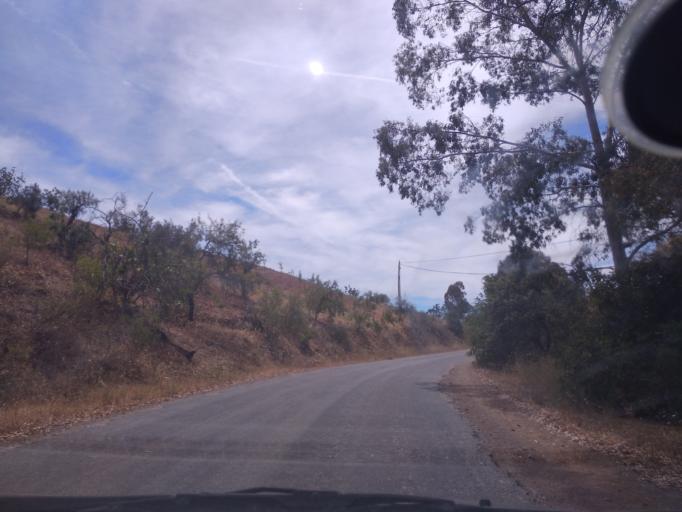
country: PT
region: Faro
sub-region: Olhao
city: Moncarapacho
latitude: 37.1620
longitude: -7.7984
